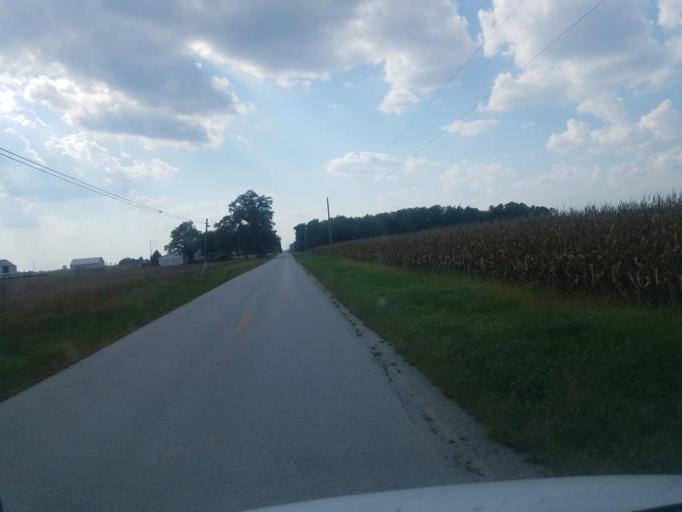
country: US
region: Ohio
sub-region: Hancock County
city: Arlington
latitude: 40.7906
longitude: -83.6809
